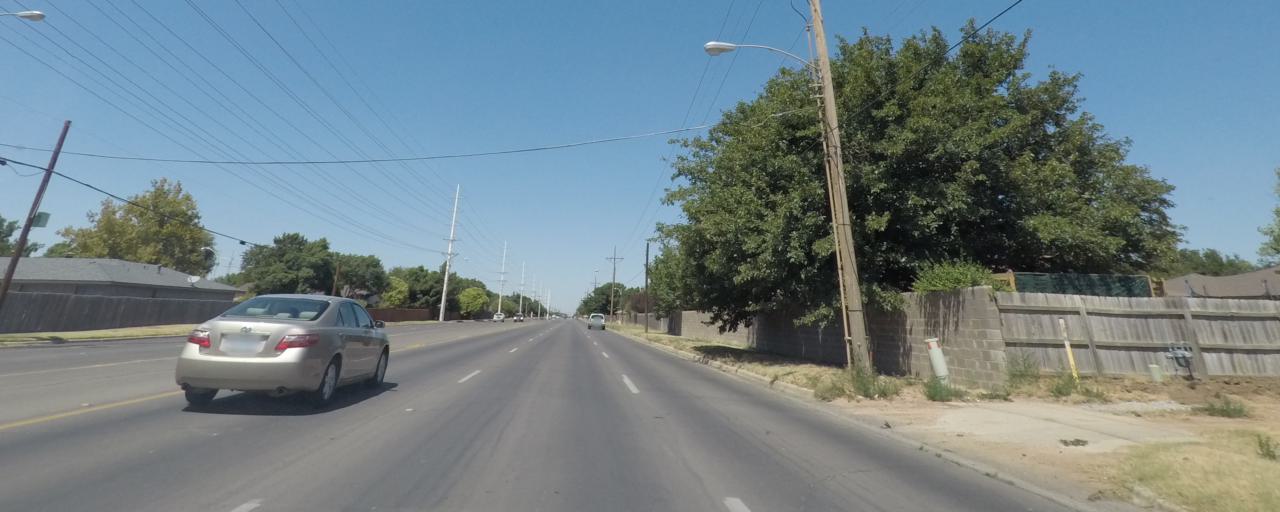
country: US
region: Texas
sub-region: Lubbock County
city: Lubbock
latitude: 33.5128
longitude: -101.8876
